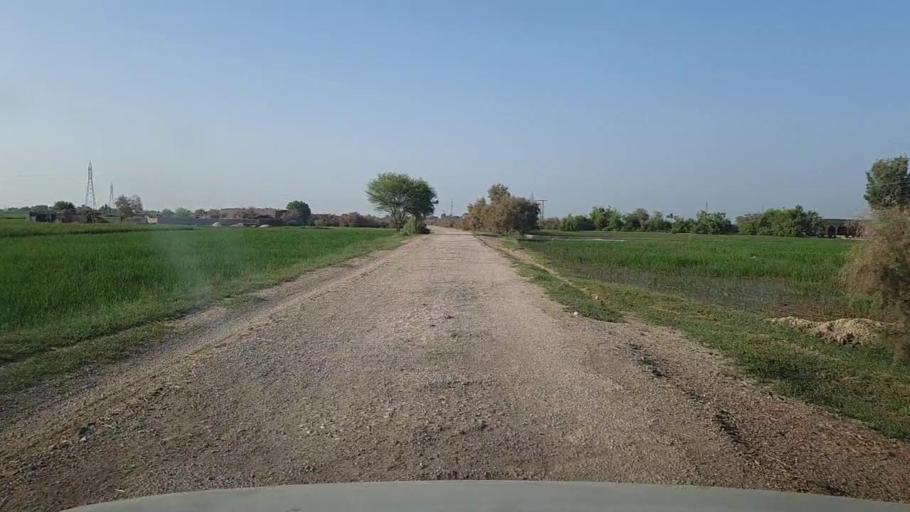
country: PK
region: Sindh
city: Kandhkot
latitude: 28.3033
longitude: 69.3288
